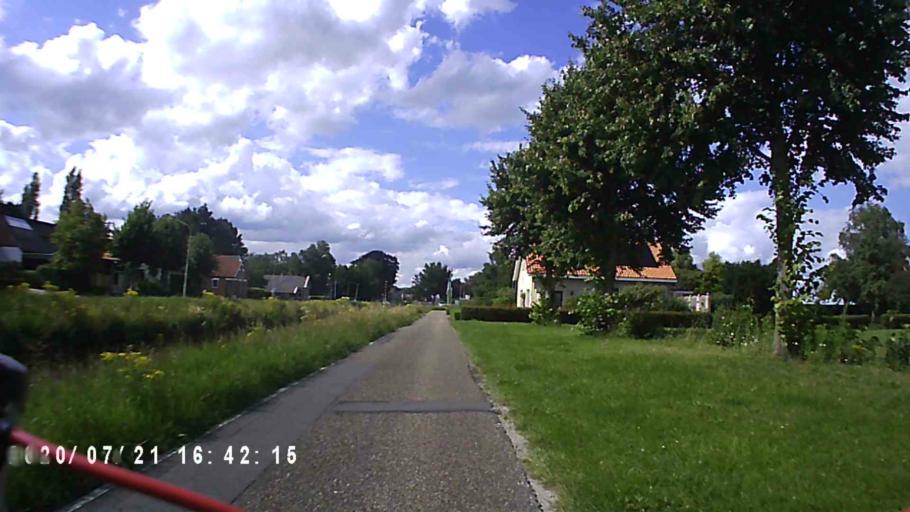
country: NL
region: Groningen
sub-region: Gemeente Hoogezand-Sappemeer
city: Sappemeer
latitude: 53.1031
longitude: 6.7865
